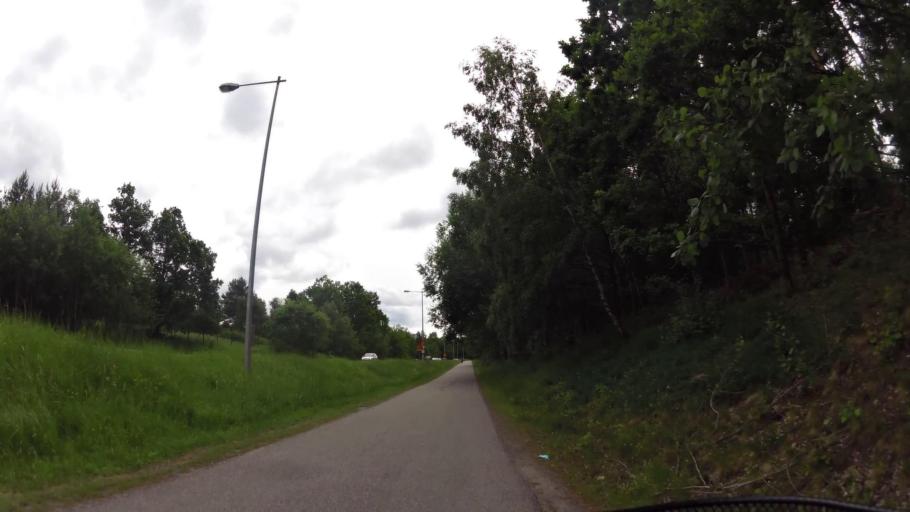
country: SE
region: OEstergoetland
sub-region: Linkopings Kommun
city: Linkoping
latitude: 58.3974
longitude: 15.6060
